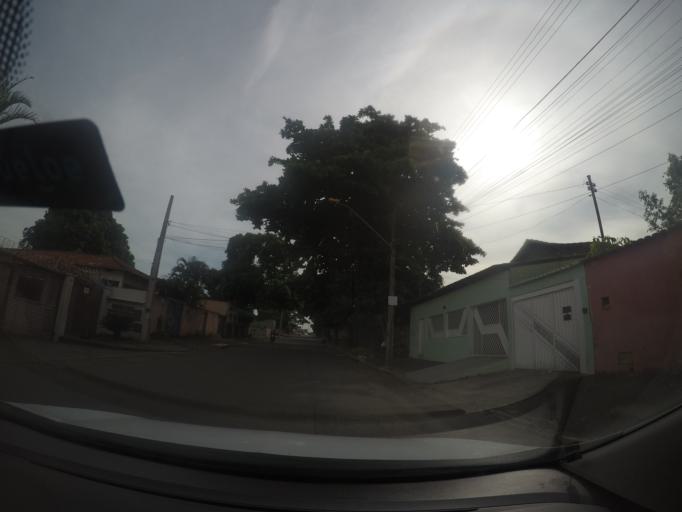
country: BR
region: Goias
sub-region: Goiania
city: Goiania
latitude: -16.6582
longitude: -49.3059
